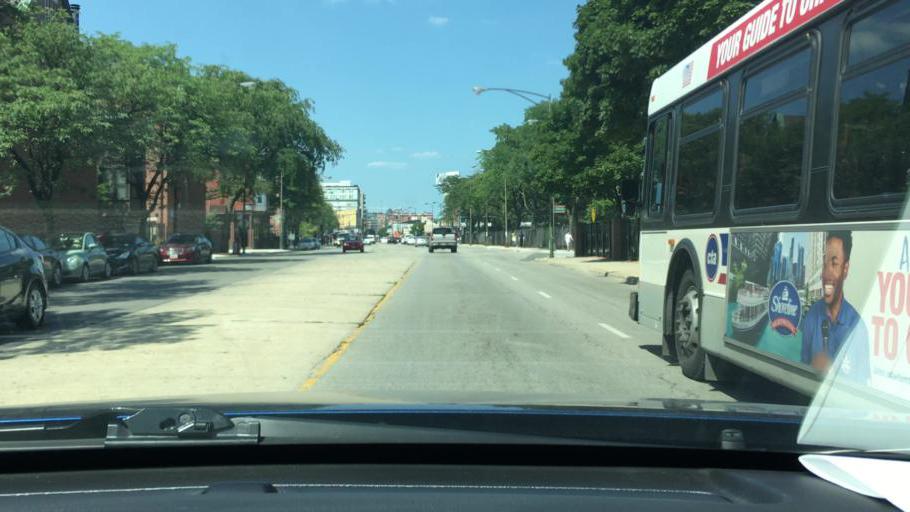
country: US
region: Illinois
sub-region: Cook County
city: Chicago
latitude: 41.8724
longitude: -87.6568
